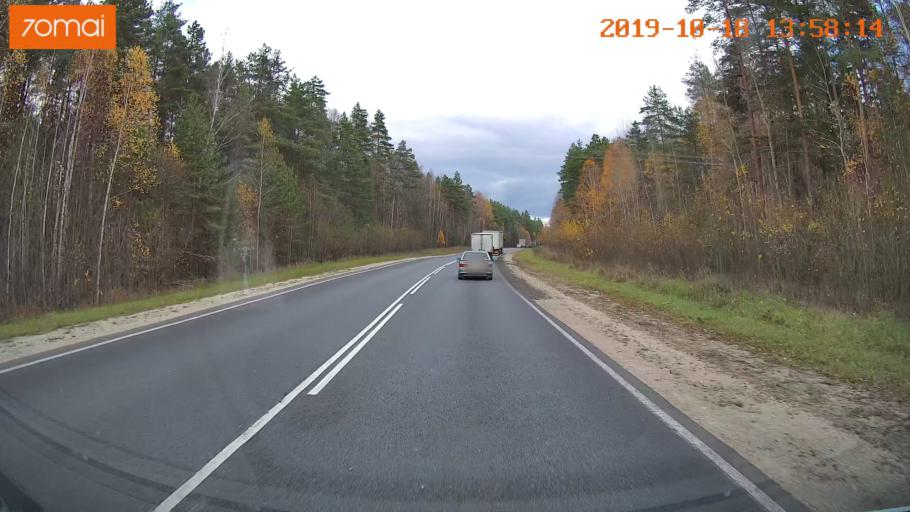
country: RU
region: Rjazan
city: Spas-Klepiki
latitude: 55.0827
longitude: 40.0529
